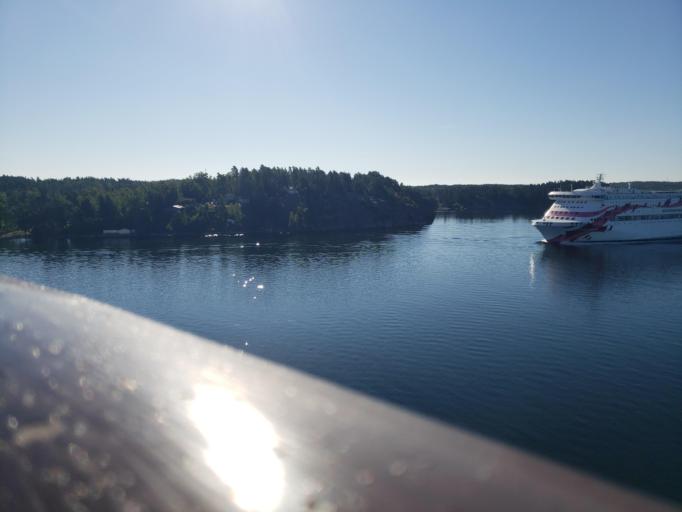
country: SE
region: Stockholm
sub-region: Varmdo Kommun
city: Mortnas
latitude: 59.3857
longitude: 18.4435
